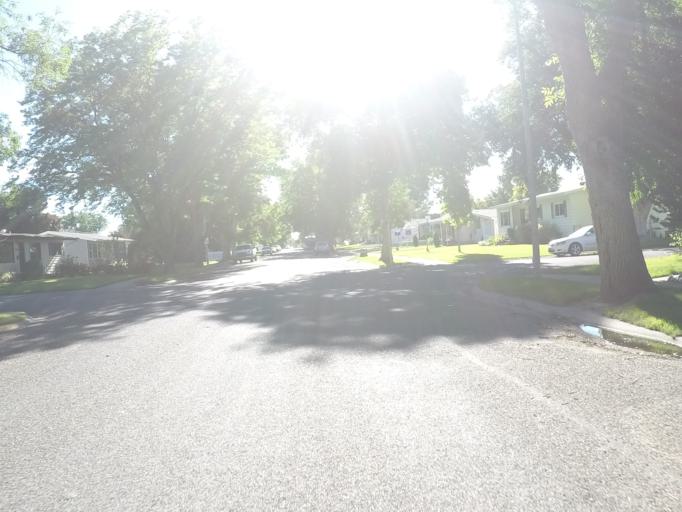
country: US
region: Montana
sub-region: Yellowstone County
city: Billings
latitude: 45.7737
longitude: -108.5786
